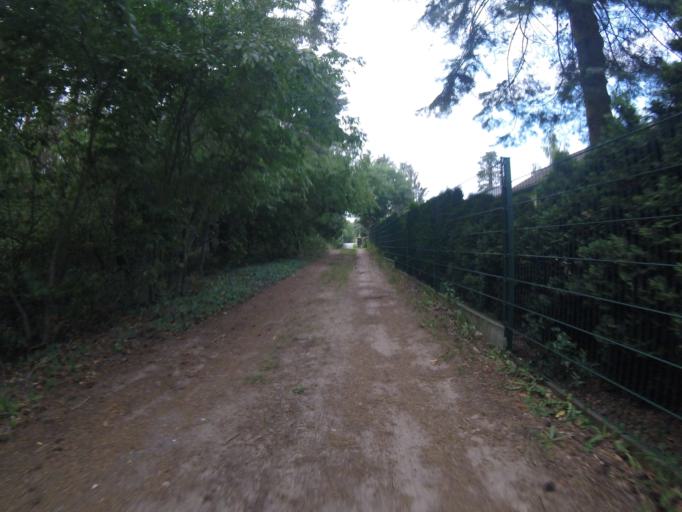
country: DE
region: Brandenburg
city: Bestensee
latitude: 52.2484
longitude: 13.6243
